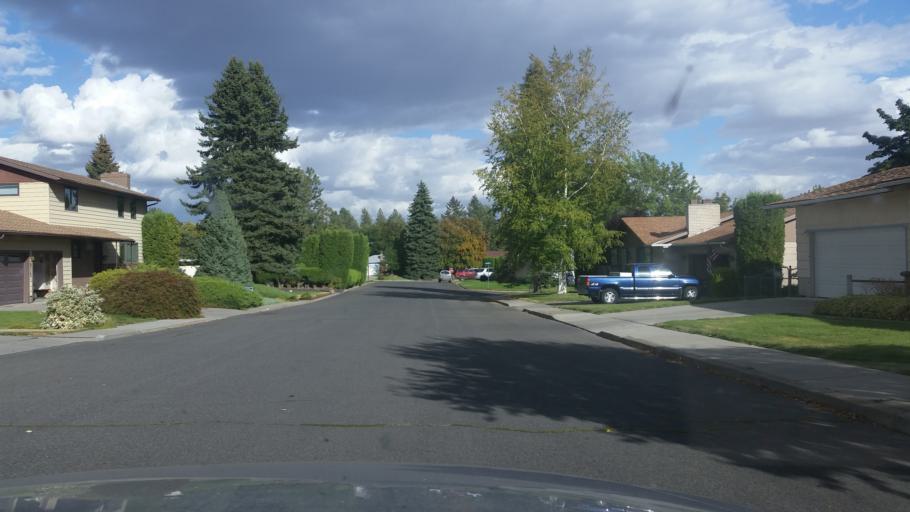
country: US
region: Washington
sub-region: Spokane County
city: Cheney
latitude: 47.4838
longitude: -117.5942
